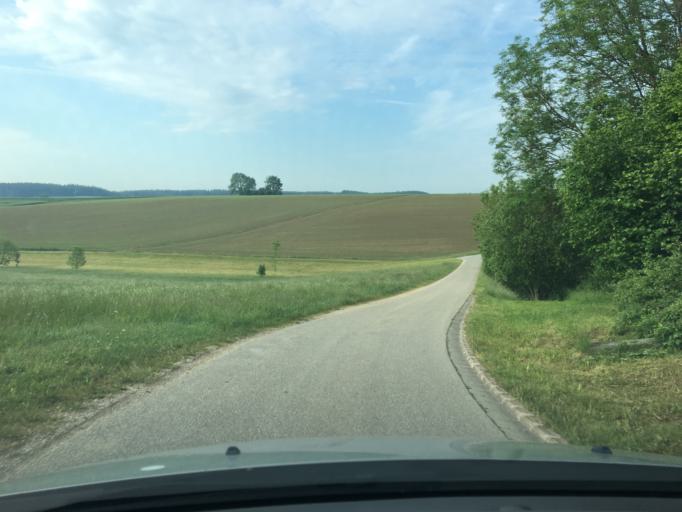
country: DE
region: Bavaria
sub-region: Upper Bavaria
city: Egglkofen
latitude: 48.4049
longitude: 12.4325
